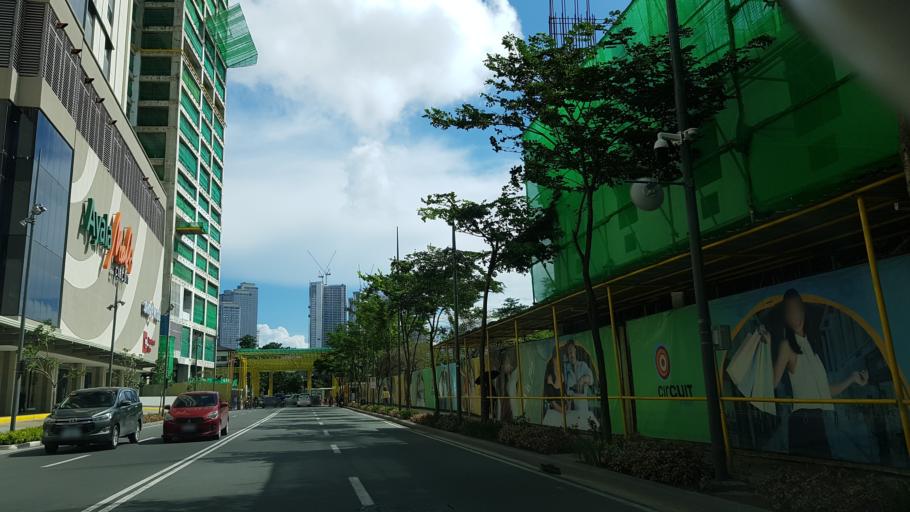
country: PH
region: Metro Manila
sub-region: Mandaluyong
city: Mandaluyong City
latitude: 14.5739
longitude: 121.0180
